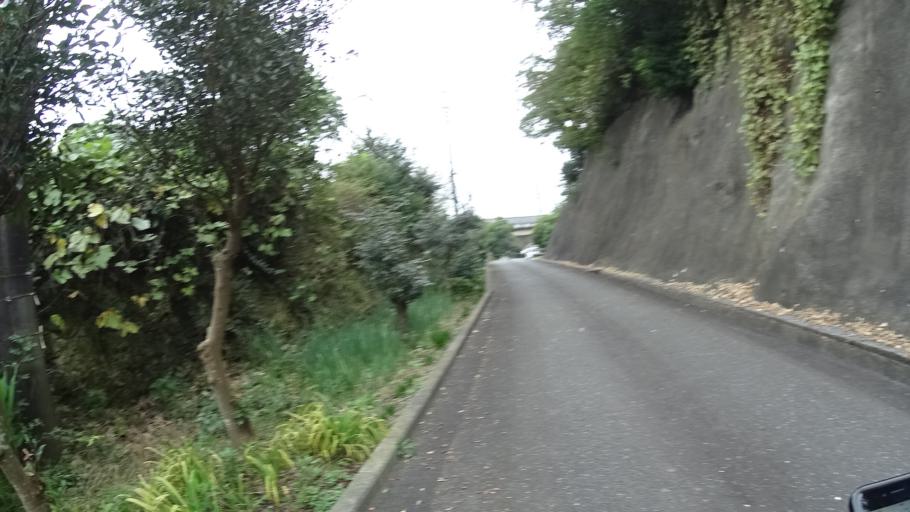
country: JP
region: Kanagawa
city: Zushi
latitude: 35.2946
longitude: 139.6197
